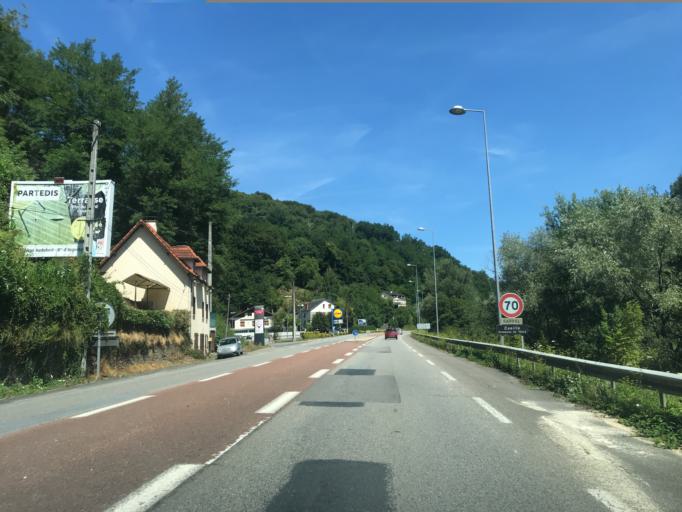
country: FR
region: Limousin
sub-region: Departement de la Correze
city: Tulle
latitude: 45.2463
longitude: 1.7460
